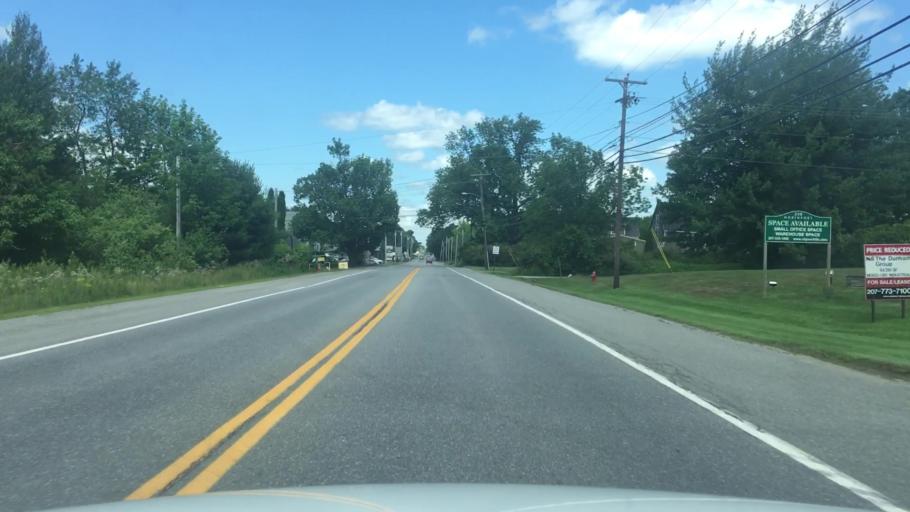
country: US
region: Maine
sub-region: Waldo County
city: Belfast
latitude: 44.3999
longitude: -68.9876
